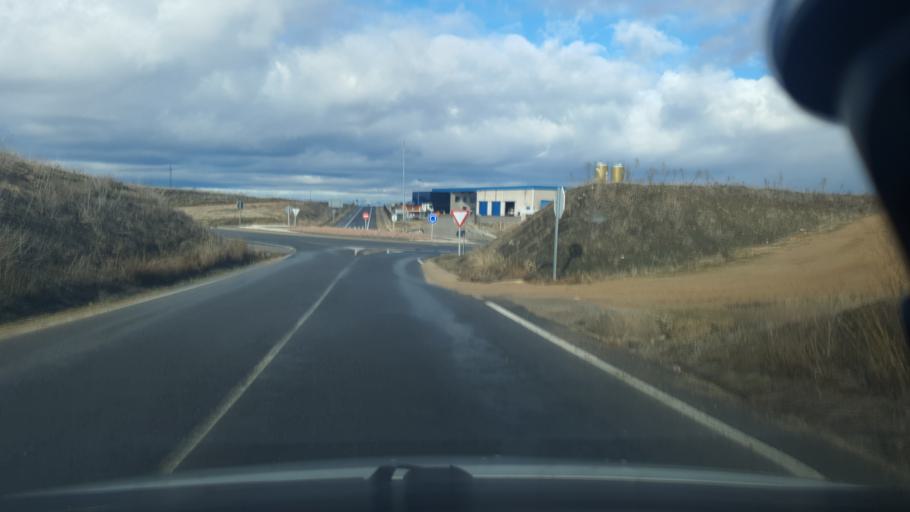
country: ES
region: Castille and Leon
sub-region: Provincia de Segovia
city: Carbonero el Mayor
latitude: 41.1395
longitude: -4.2695
